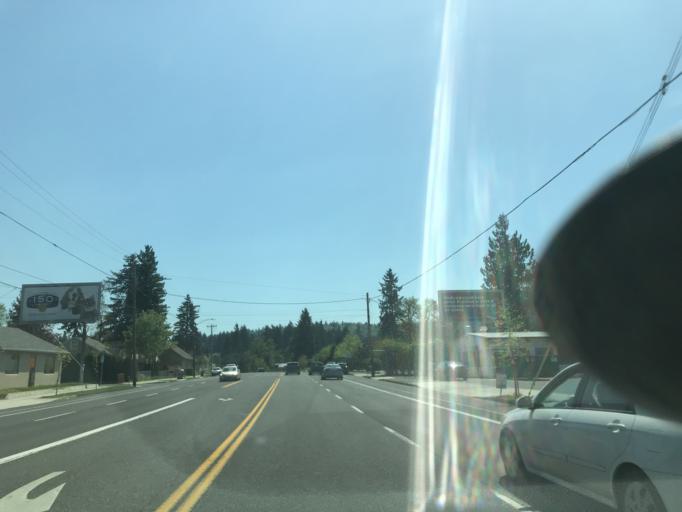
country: US
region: Oregon
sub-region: Multnomah County
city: Lents
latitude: 45.4832
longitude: -122.5380
